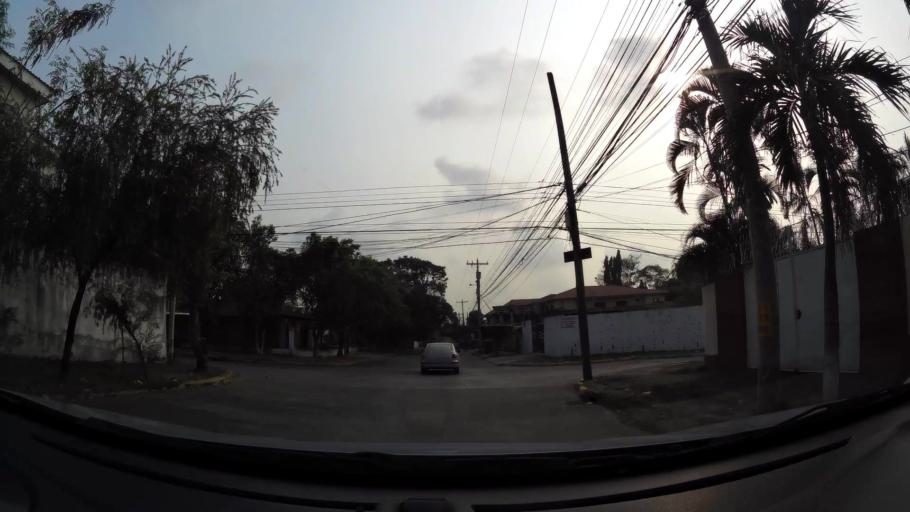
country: HN
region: Cortes
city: Armenta
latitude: 15.4927
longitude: -88.0428
